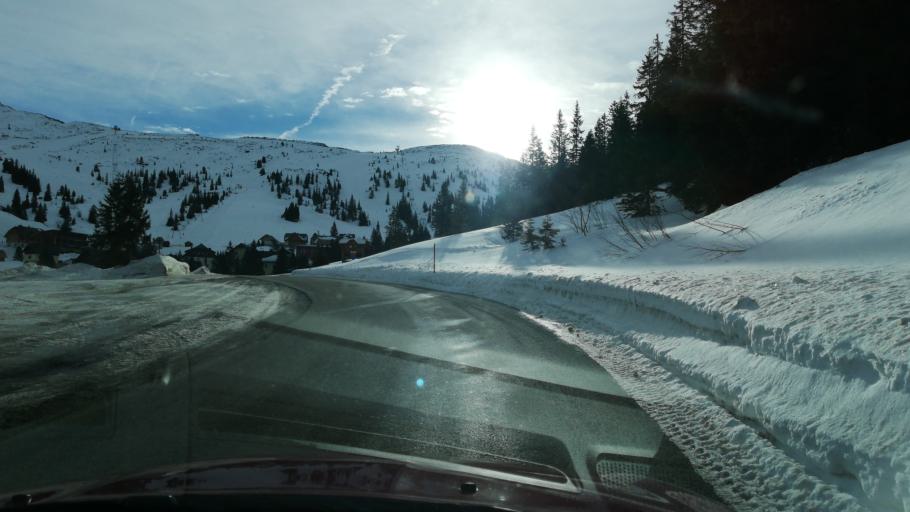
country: AT
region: Styria
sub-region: Politischer Bezirk Liezen
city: Donnersbach
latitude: 47.4065
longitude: 14.1948
